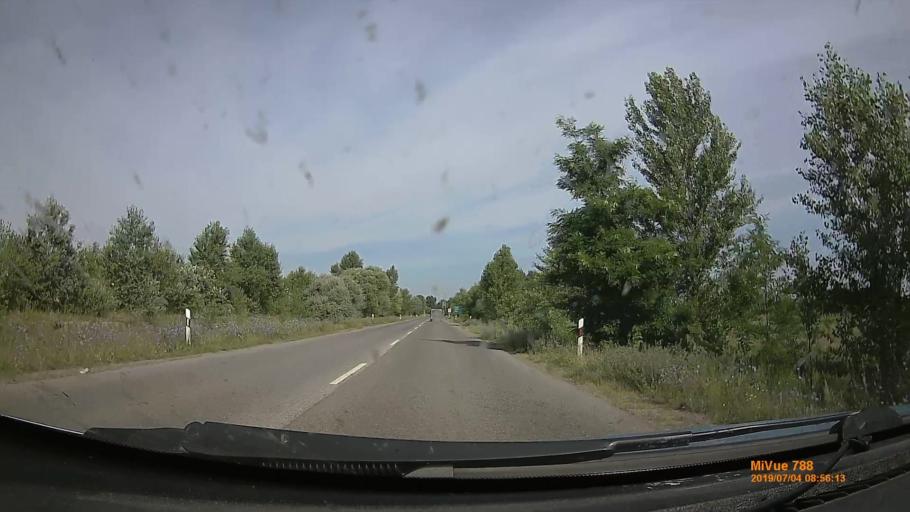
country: HU
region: Pest
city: Gyal
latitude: 47.3869
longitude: 19.2462
